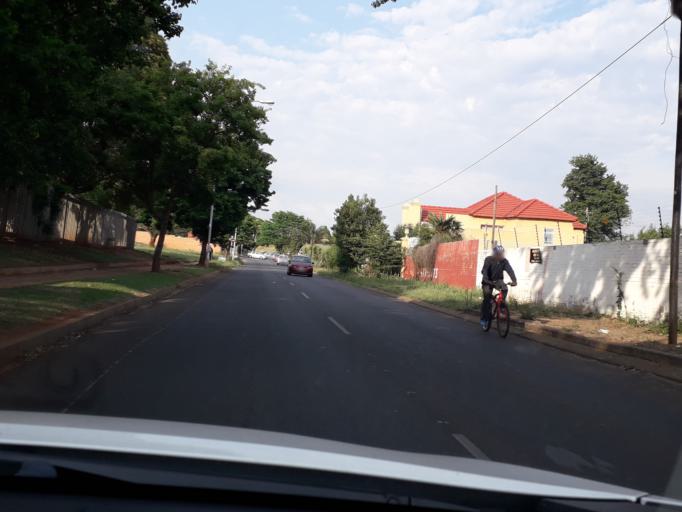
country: ZA
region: Gauteng
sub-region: City of Johannesburg Metropolitan Municipality
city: Johannesburg
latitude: -26.1653
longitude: 27.9790
